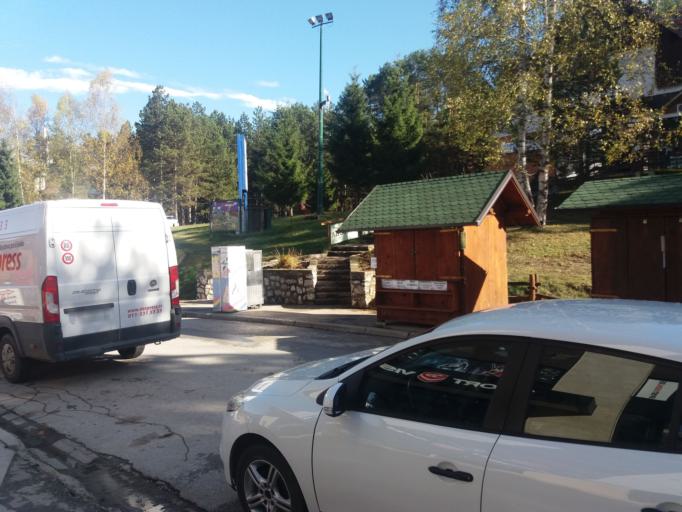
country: RS
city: Zlatibor
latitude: 43.7252
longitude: 19.6987
